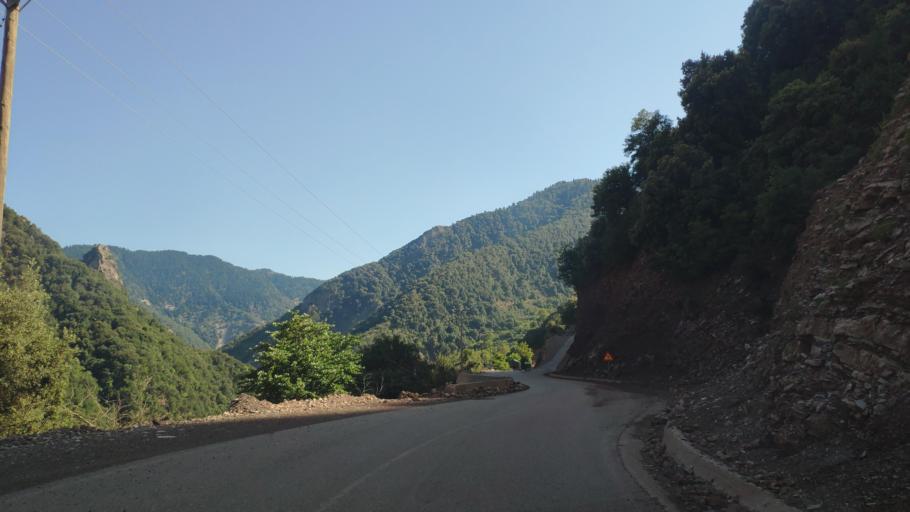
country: GR
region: Central Greece
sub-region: Nomos Evrytanias
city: Kerasochori
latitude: 39.0836
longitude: 21.5966
